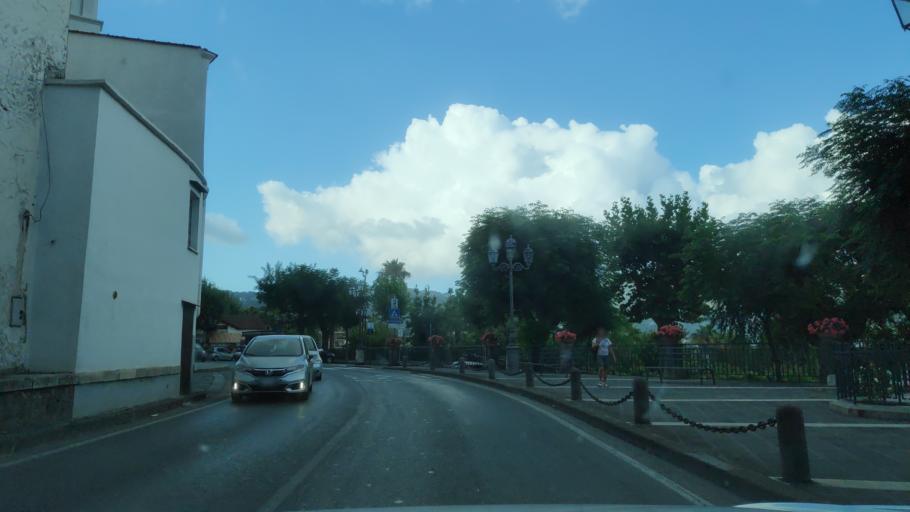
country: IT
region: Campania
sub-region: Provincia di Napoli
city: Meta
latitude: 40.6424
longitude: 14.4175
